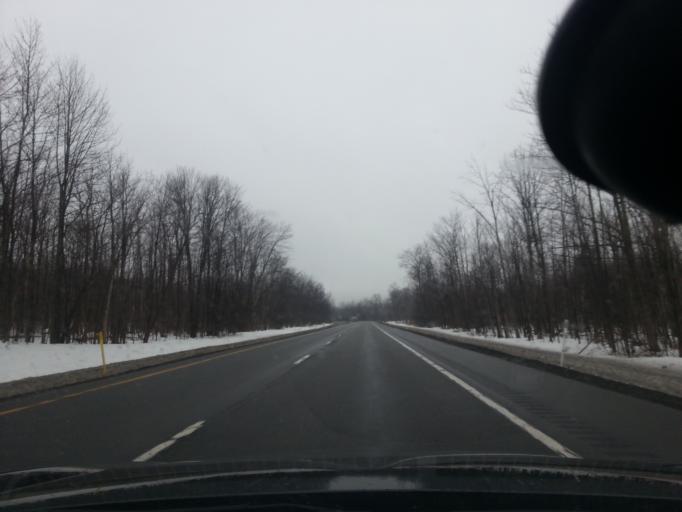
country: US
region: New York
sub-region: Jefferson County
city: Adams
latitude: 43.7466
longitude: -76.0686
